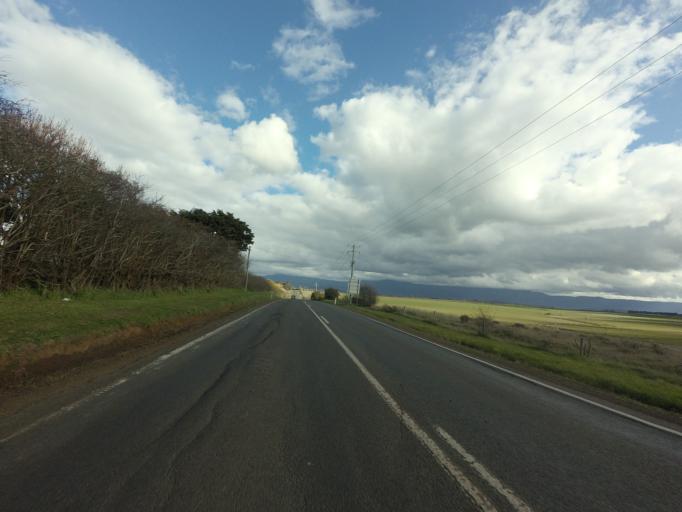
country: AU
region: Tasmania
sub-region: Northern Midlands
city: Longford
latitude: -41.6966
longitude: 147.0780
